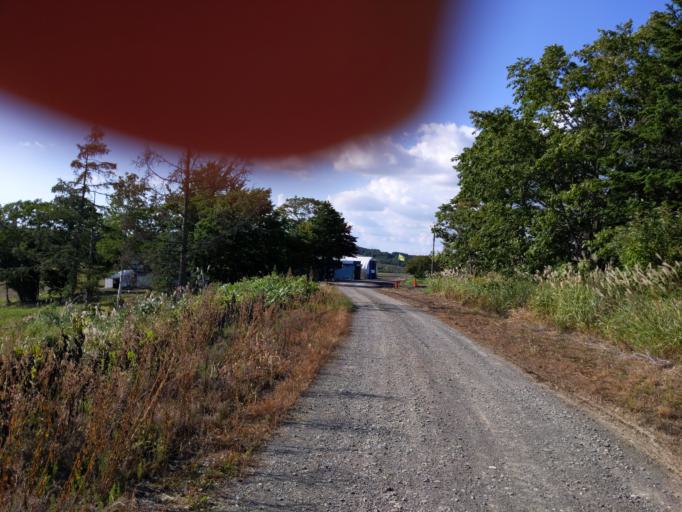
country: JP
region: Hokkaido
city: Iwamizawa
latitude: 43.1949
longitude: 141.8297
